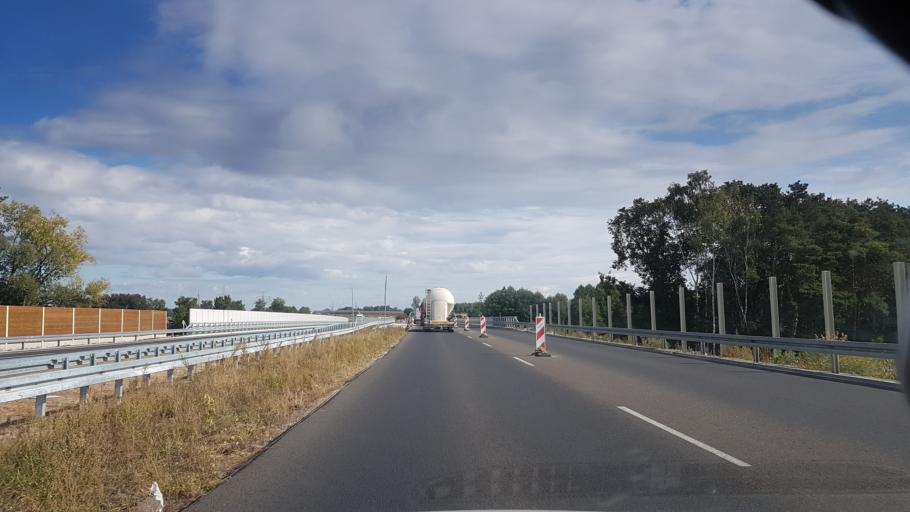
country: PL
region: Greater Poland Voivodeship
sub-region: Powiat poznanski
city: Steszew
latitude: 52.2978
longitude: 16.6905
